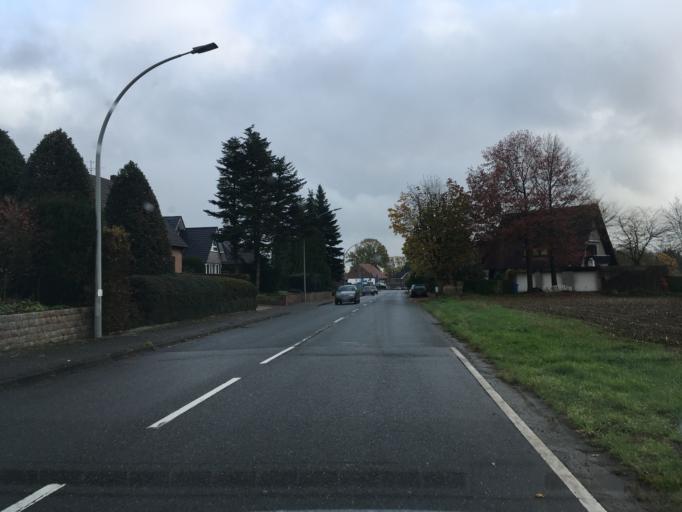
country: DE
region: North Rhine-Westphalia
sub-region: Regierungsbezirk Munster
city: Klein Reken
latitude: 51.8349
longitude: 7.0373
